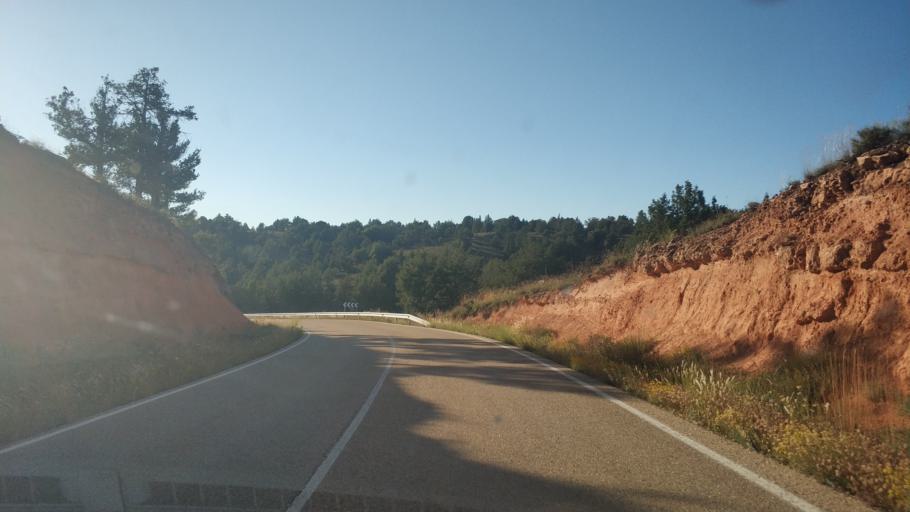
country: ES
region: Castille and Leon
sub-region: Provincia de Soria
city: Montejo de Tiermes
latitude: 41.4337
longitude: -3.2051
